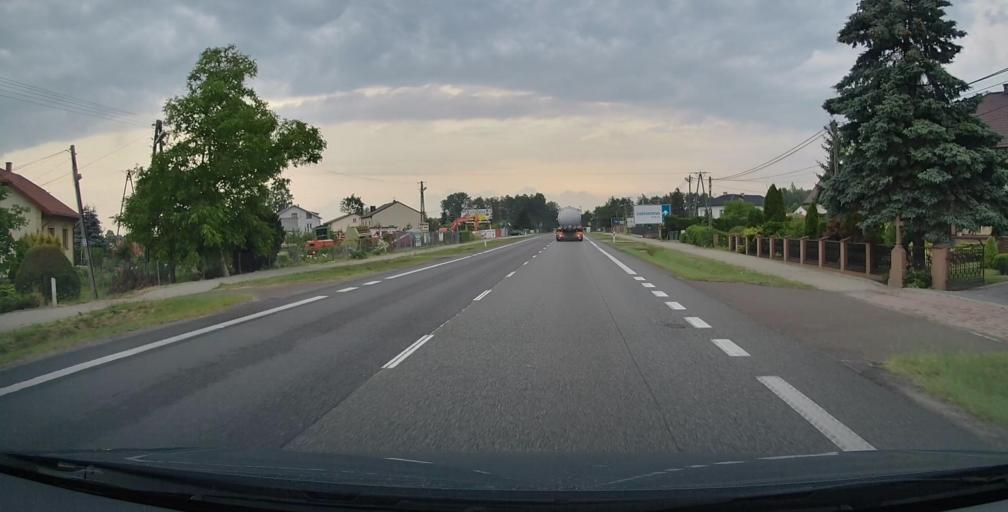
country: PL
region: Masovian Voivodeship
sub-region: Powiat siedlecki
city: Zbuczyn
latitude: 52.0906
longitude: 22.4288
